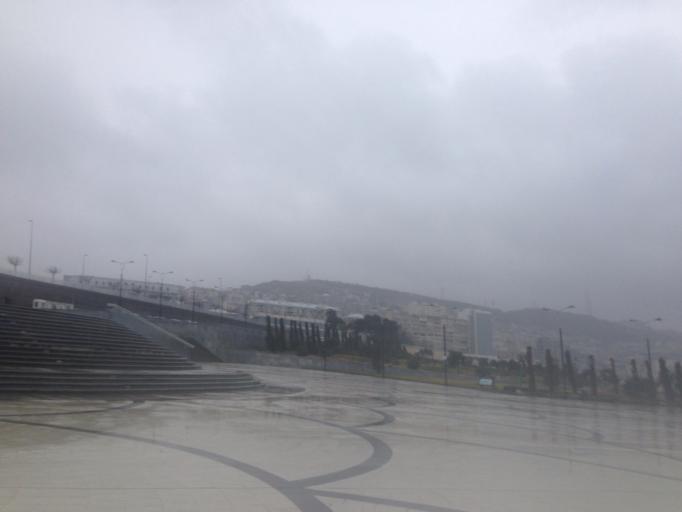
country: AZ
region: Baki
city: Badamdar
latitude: 40.3458
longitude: 49.8446
